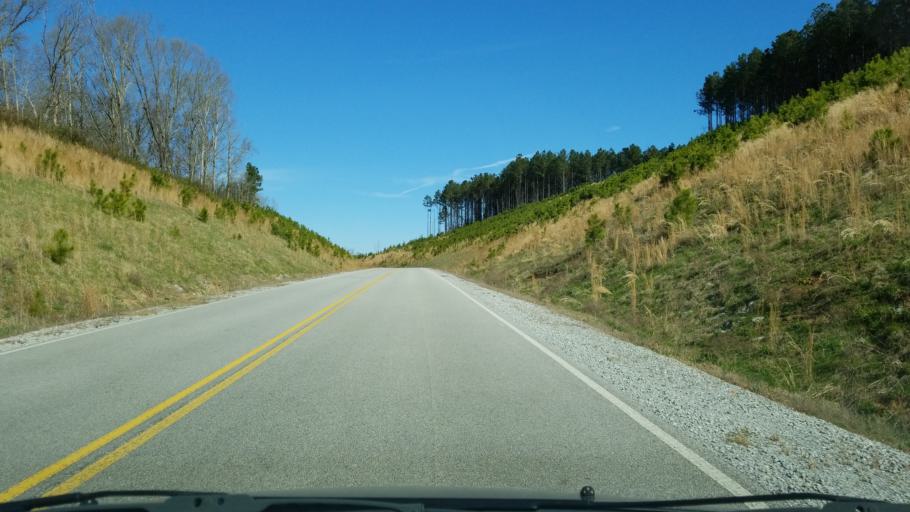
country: US
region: Tennessee
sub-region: Hamilton County
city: Harrison
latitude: 35.1013
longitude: -85.1368
